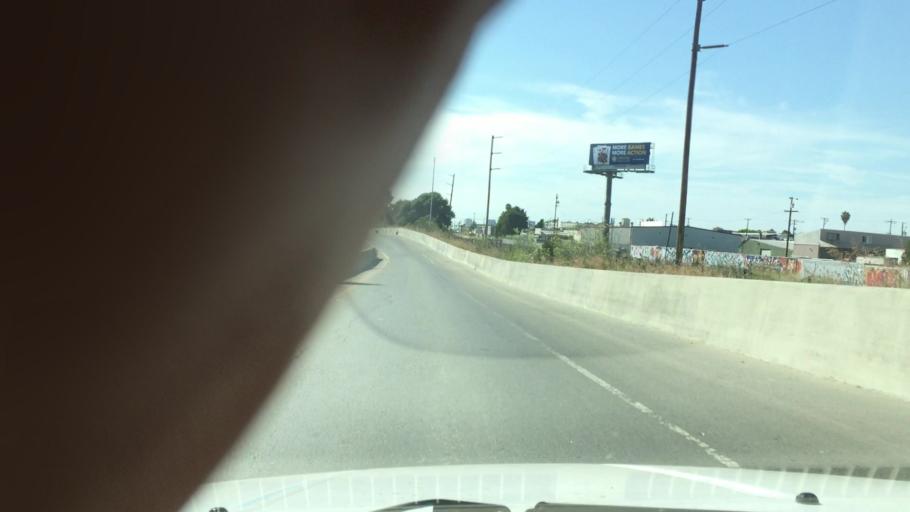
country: US
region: California
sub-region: Alameda County
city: Alameda
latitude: 37.7704
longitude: -122.2211
